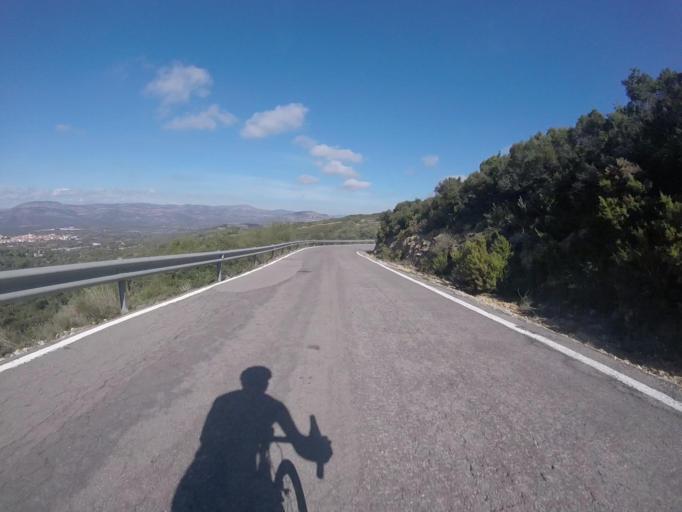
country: ES
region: Valencia
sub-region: Provincia de Castello
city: Albocasser
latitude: 40.3489
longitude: 0.0495
